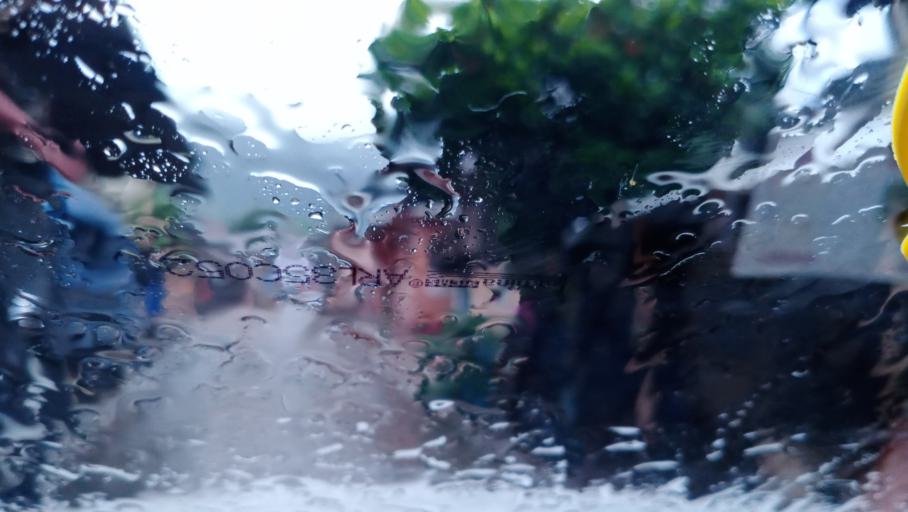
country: LA
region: Phongsali
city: Khoa
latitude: 21.0815
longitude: 102.5059
